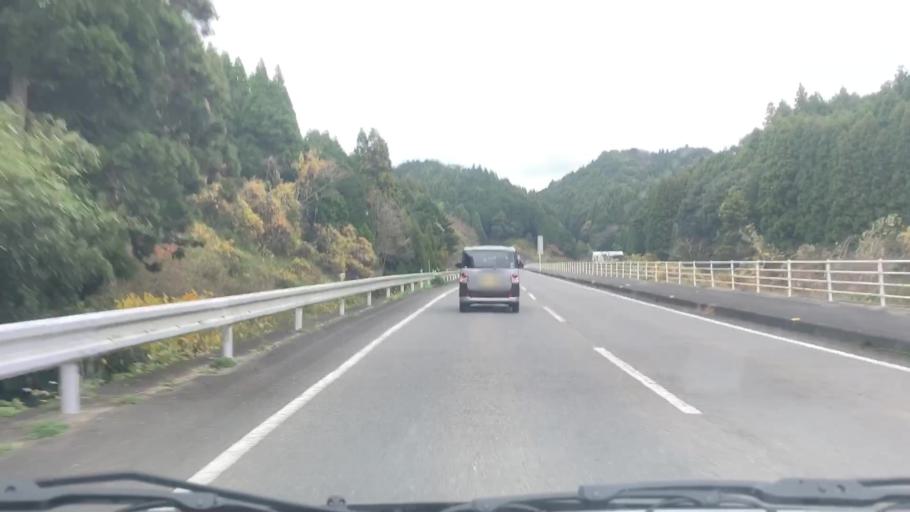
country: JP
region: Saga Prefecture
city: Ureshinomachi-shimojuku
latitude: 33.0951
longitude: 130.0304
